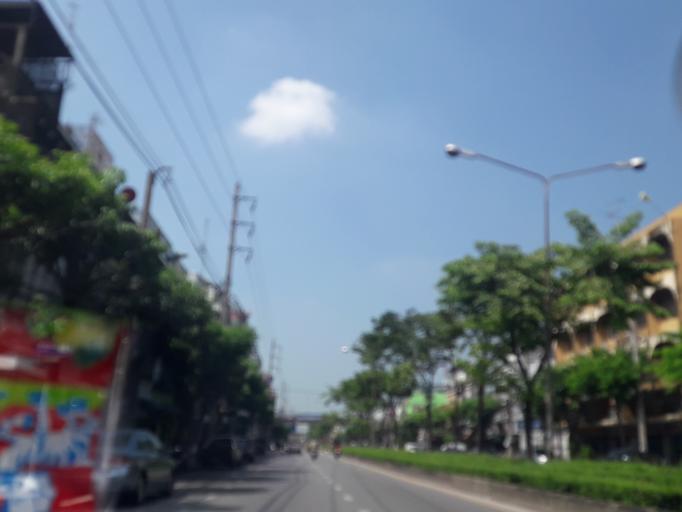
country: TH
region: Bangkok
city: Bangkok Noi
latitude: 13.7552
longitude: 100.4744
